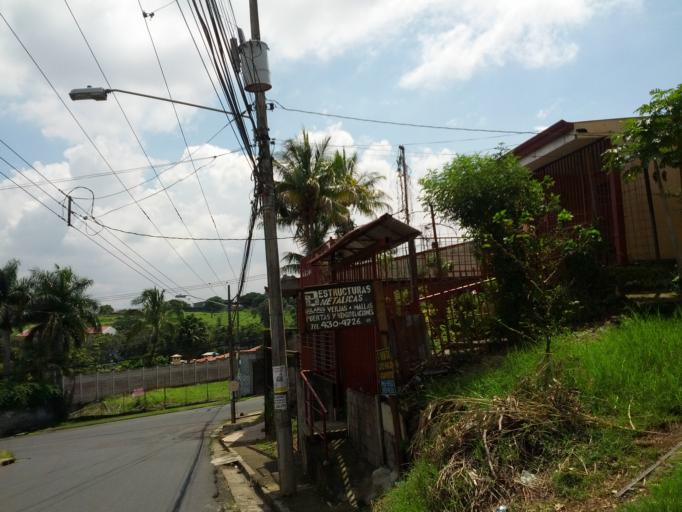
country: CR
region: Alajuela
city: Alajuela
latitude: 10.0198
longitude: -84.1994
